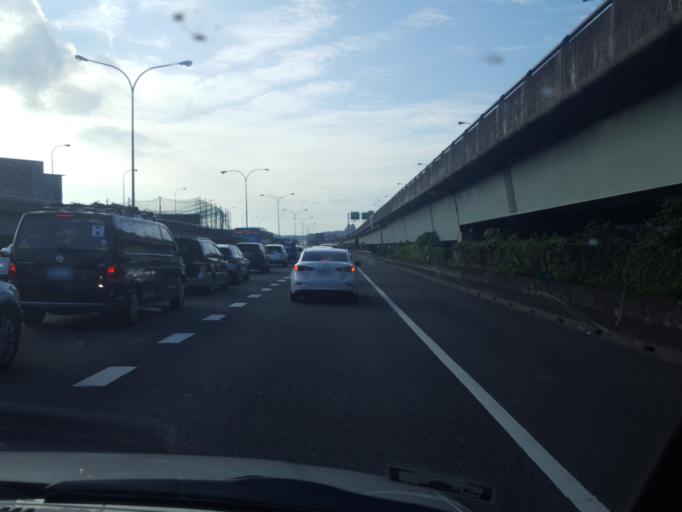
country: TW
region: Taipei
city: Taipei
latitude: 25.0676
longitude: 121.5836
